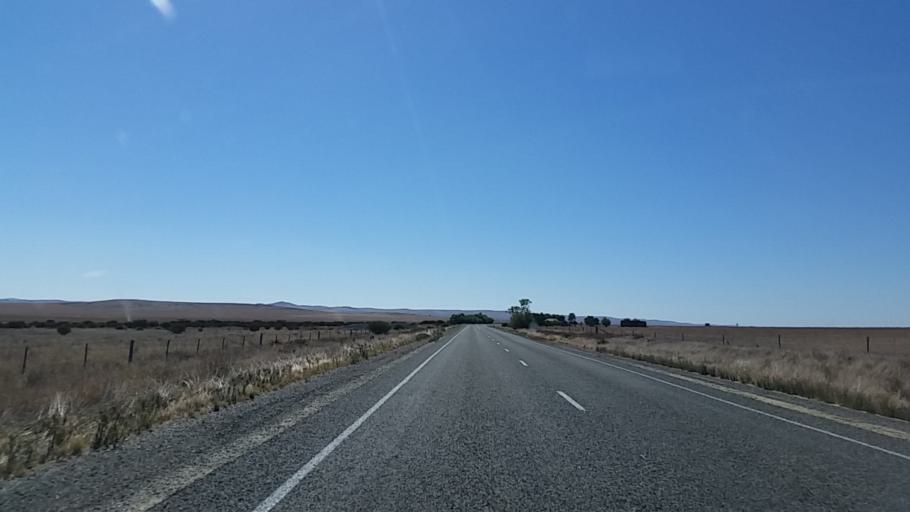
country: AU
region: South Australia
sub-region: Northern Areas
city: Jamestown
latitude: -33.2863
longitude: 138.8701
